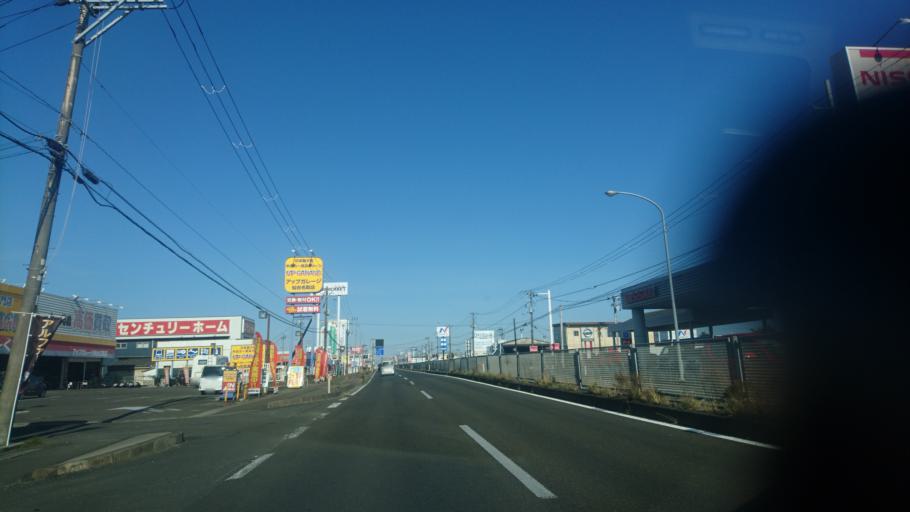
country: JP
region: Miyagi
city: Iwanuma
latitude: 38.1507
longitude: 140.8846
